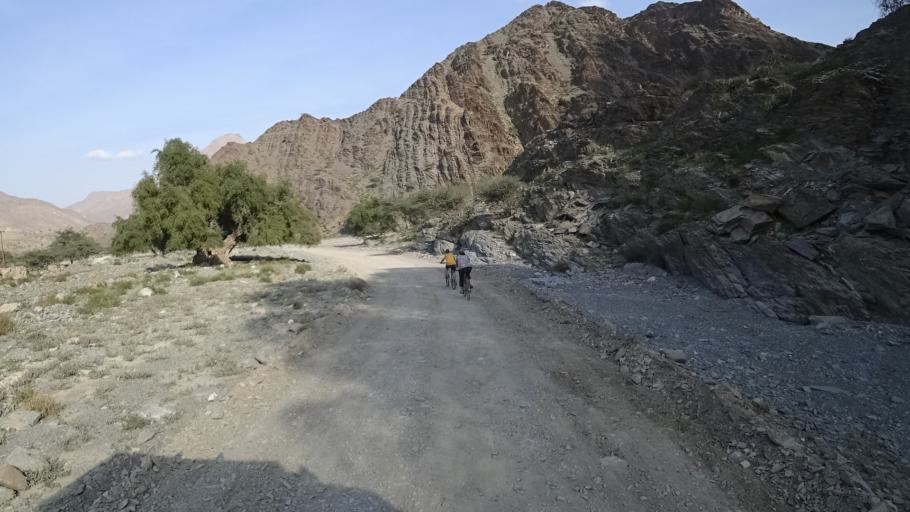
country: OM
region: Al Batinah
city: Bayt al `Awabi
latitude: 23.2560
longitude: 57.4285
